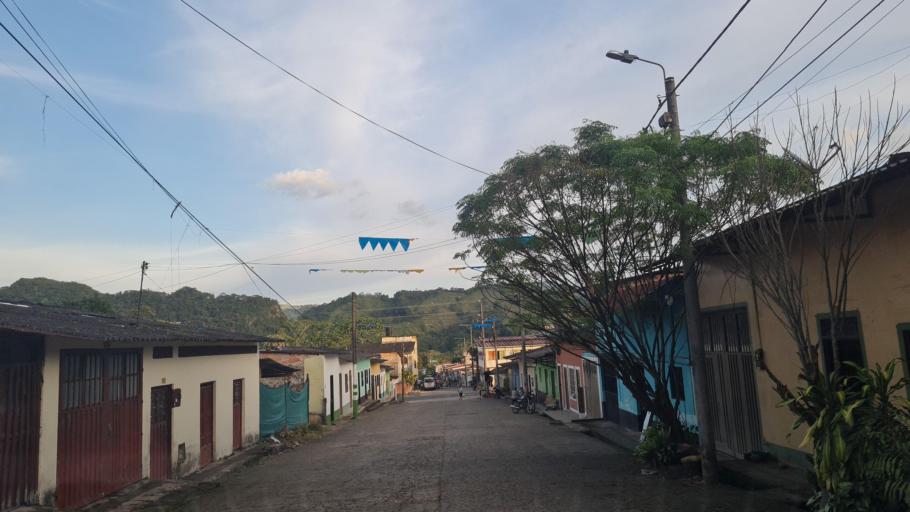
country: CO
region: Boyaca
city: San Luis de Gaceno
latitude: 4.8216
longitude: -73.1697
